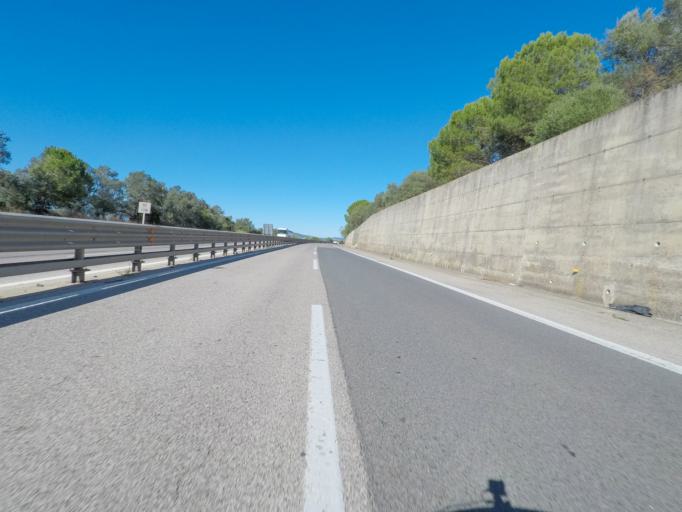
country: IT
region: Tuscany
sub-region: Provincia di Grosseto
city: Grosseto
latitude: 42.7367
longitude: 11.1373
